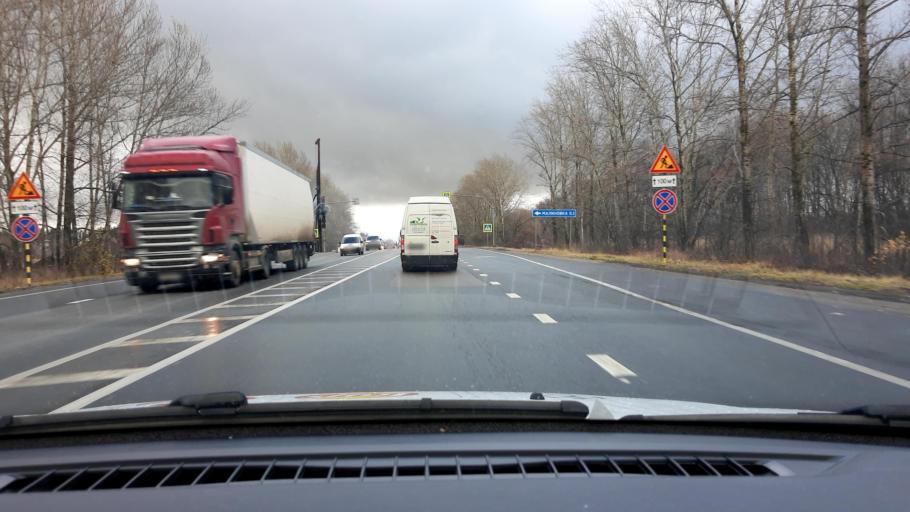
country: RU
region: Nizjnij Novgorod
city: Pamyat' Parizhskoy Kommuny
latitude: 56.0011
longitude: 44.6357
